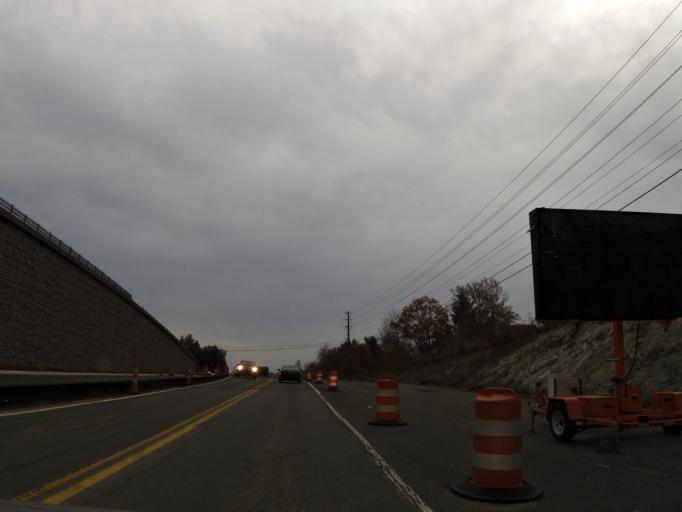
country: US
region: North Carolina
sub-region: Watauga County
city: Blowing Rock
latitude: 36.1376
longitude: -81.6703
